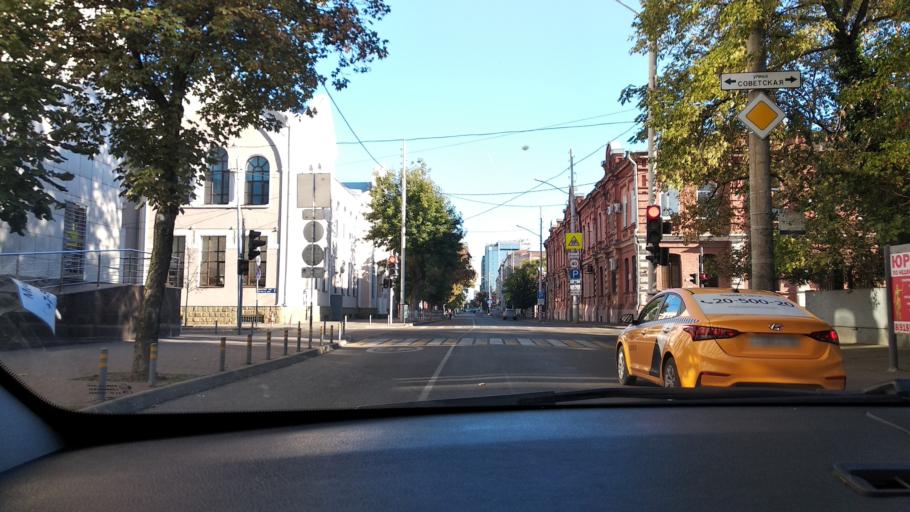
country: RU
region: Krasnodarskiy
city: Krasnodar
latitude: 45.0172
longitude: 38.9702
